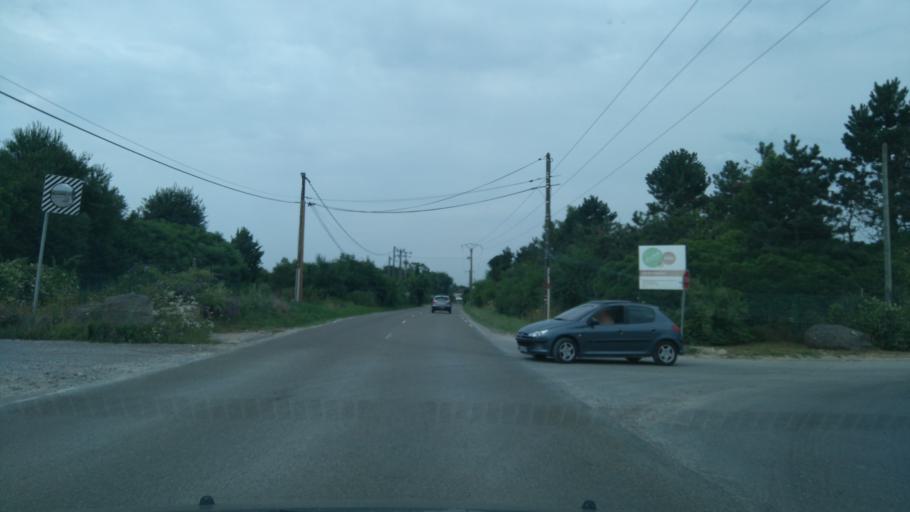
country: FR
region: Picardie
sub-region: Departement de l'Oise
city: Saint-Maximin
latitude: 49.2136
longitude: 2.4472
